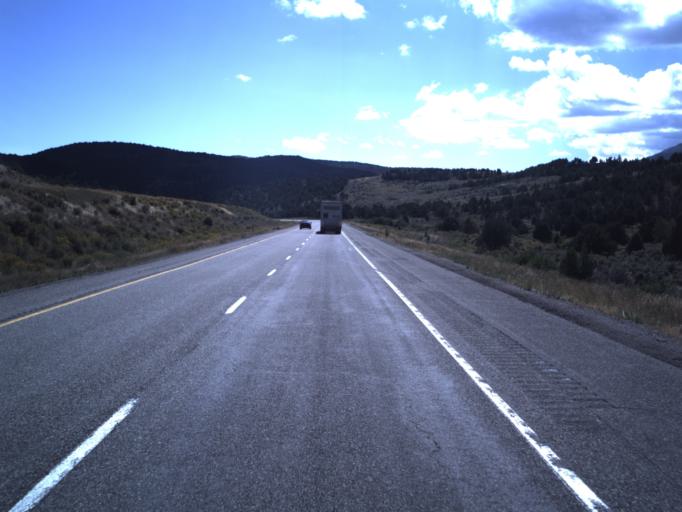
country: US
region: Utah
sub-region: Sevier County
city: Salina
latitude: 38.8572
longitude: -111.5517
